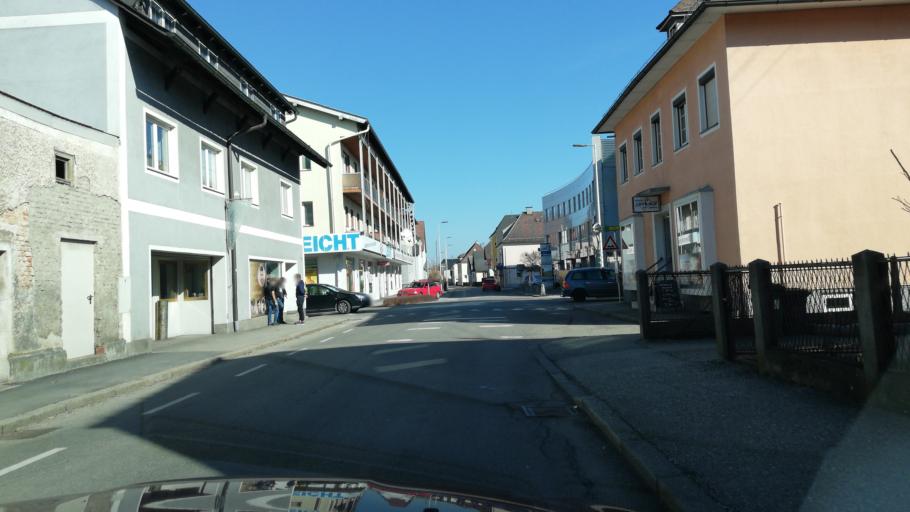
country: AT
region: Upper Austria
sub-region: Politischer Bezirk Vocklabruck
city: Attnang-Puchheim
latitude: 48.0111
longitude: 13.7234
